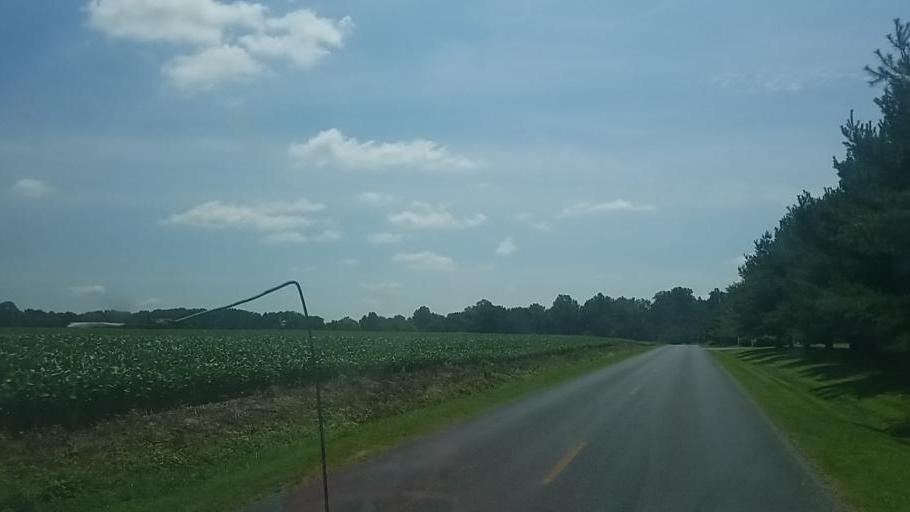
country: US
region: Maryland
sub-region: Caroline County
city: Ridgely
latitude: 38.9136
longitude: -75.9378
